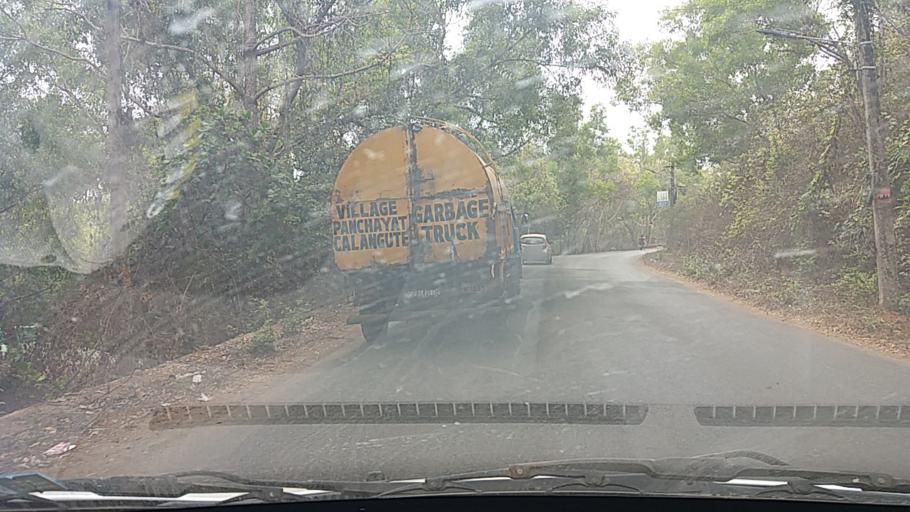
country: IN
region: Goa
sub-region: North Goa
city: Saligao
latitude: 15.5387
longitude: 73.7936
